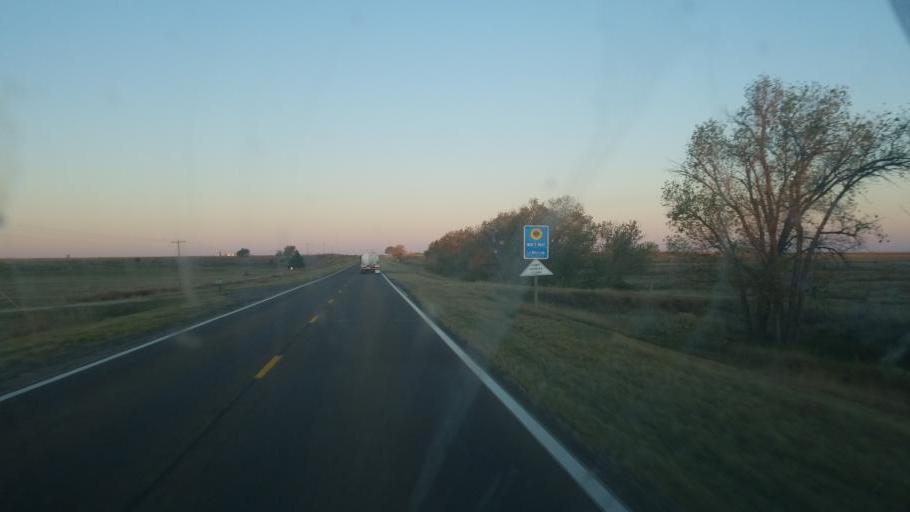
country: US
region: Kansas
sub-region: Wallace County
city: Sharon Springs
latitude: 38.9022
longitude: -101.7001
